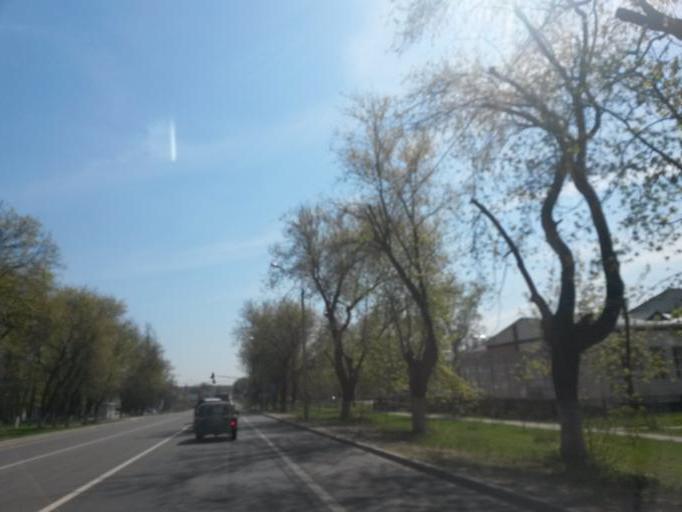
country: RU
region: Moskovskaya
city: L'vovskiy
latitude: 55.3138
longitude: 37.5286
